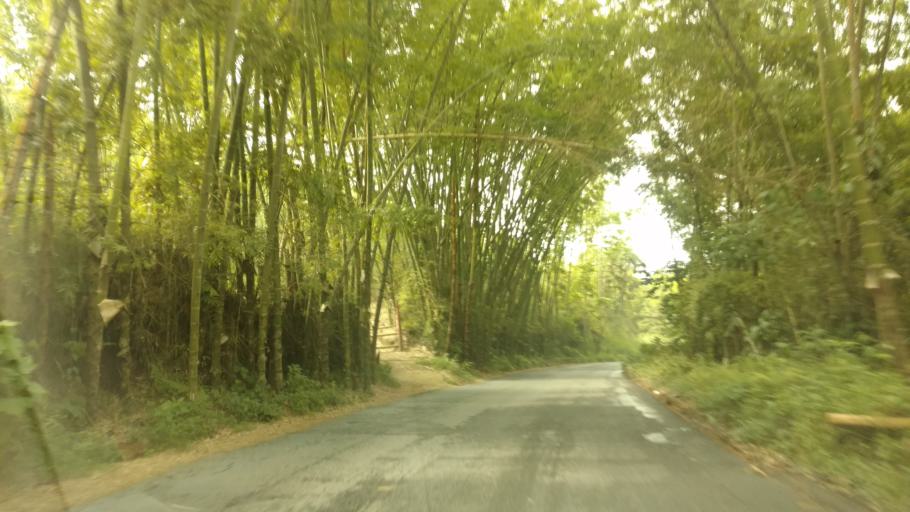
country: CO
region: Caldas
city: Neira
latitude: 5.1765
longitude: -75.5260
